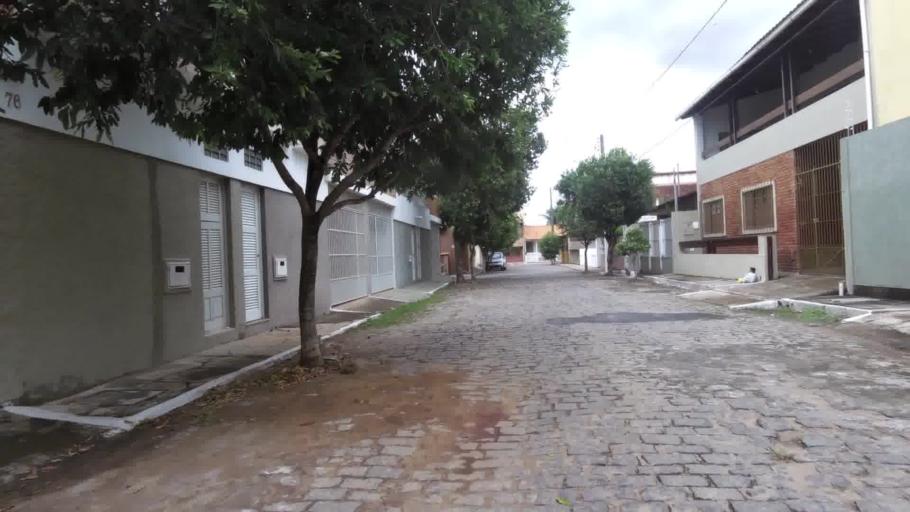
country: BR
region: Espirito Santo
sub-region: Marataizes
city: Marataizes
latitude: -21.0416
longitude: -40.8258
